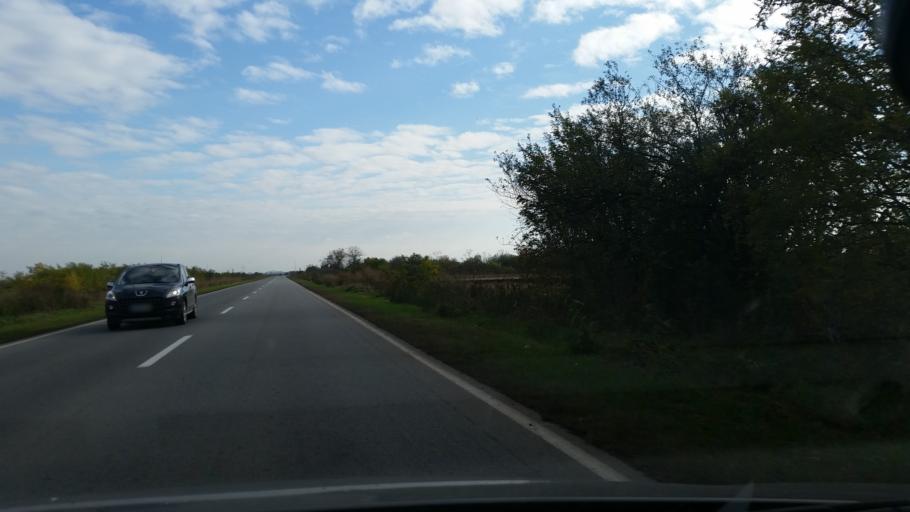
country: RS
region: Autonomna Pokrajina Vojvodina
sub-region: Srednjebanatski Okrug
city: Zrenjanin
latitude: 45.4311
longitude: 20.3682
